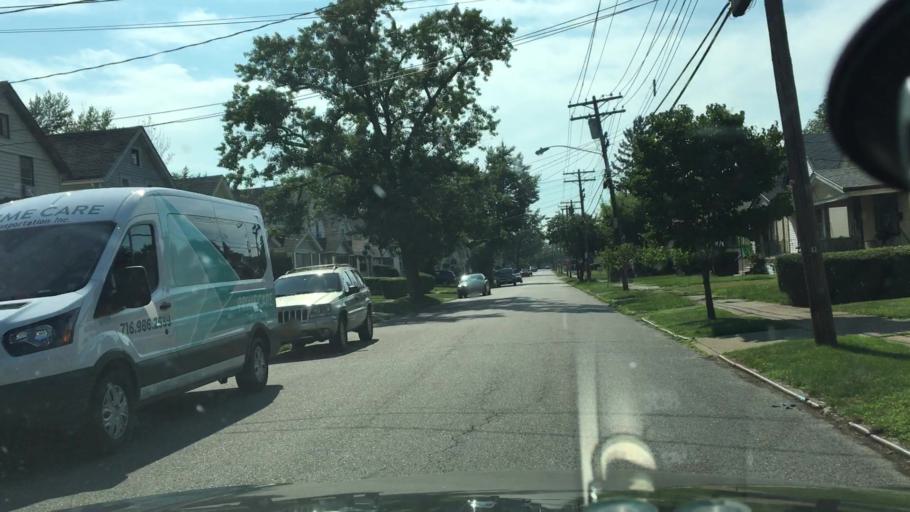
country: US
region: New York
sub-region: Erie County
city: Eggertsville
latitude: 42.9366
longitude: -78.8087
